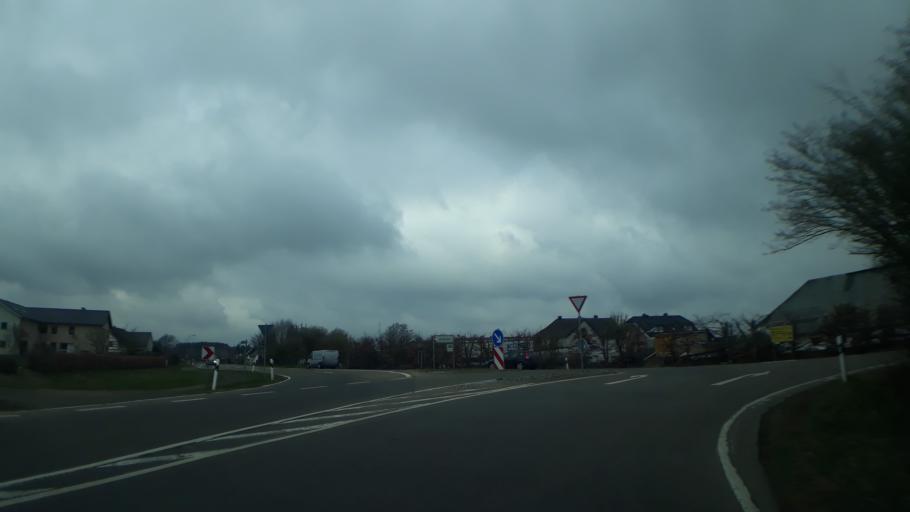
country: DE
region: North Rhine-Westphalia
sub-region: Regierungsbezirk Koln
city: Schleiden
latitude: 50.5551
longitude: 6.4568
